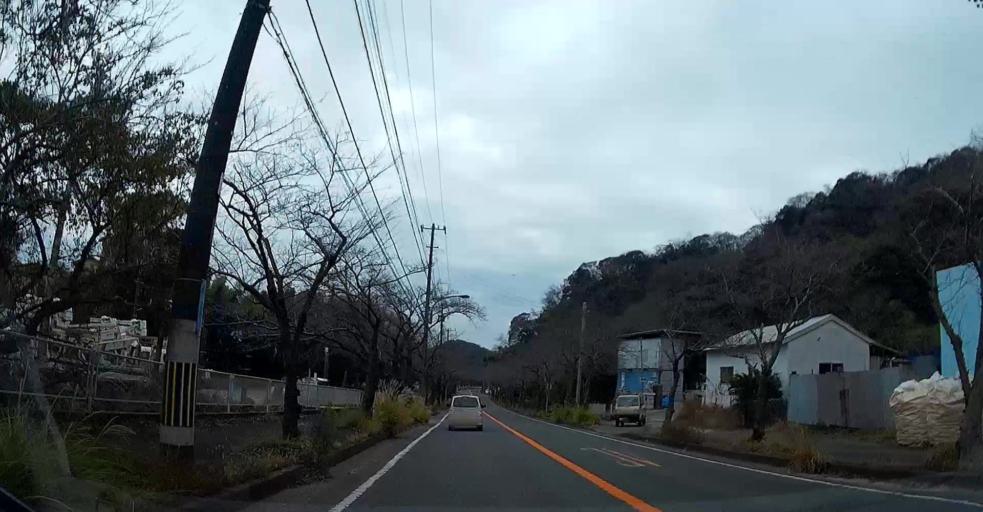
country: JP
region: Kanagawa
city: Yokosuka
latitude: 35.2198
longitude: 139.6693
